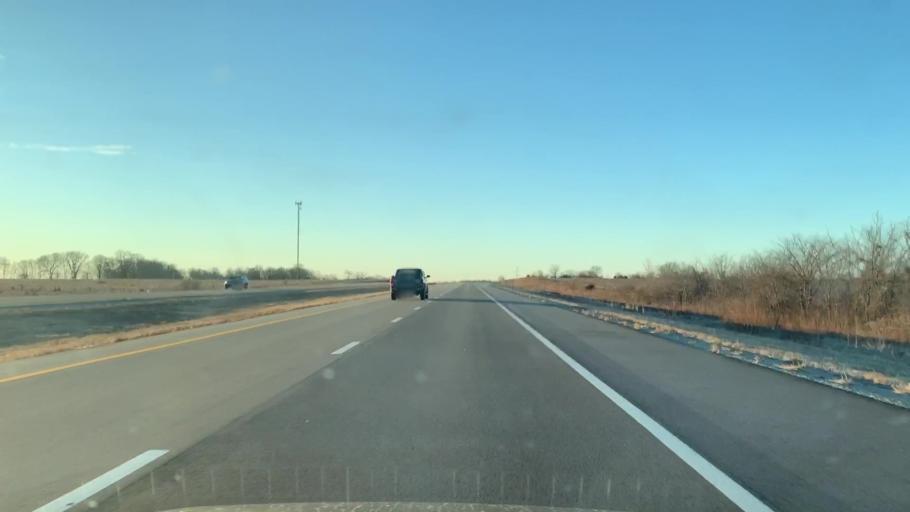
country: US
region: Kansas
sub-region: Linn County
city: La Cygne
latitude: 38.3714
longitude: -94.6877
